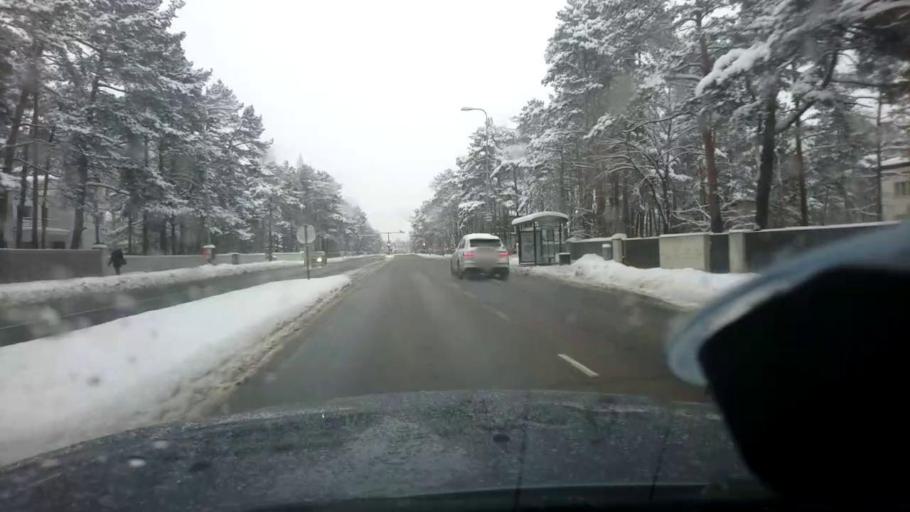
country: EE
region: Harju
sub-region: Tallinna linn
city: Tallinn
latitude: 59.3855
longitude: 24.7115
